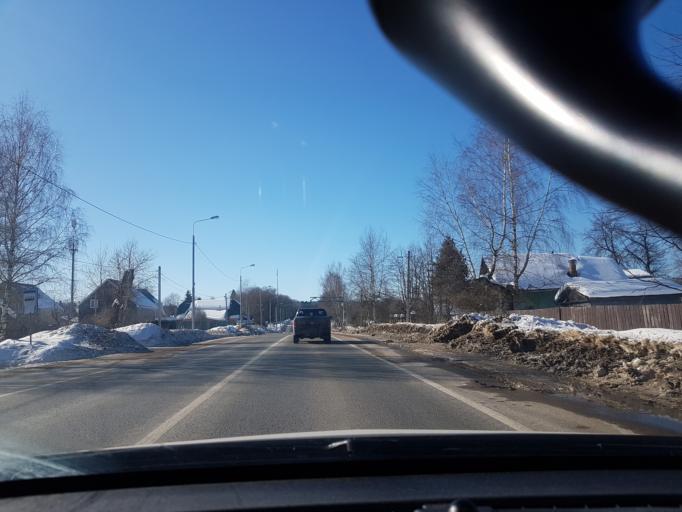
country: RU
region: Moskovskaya
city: Kostrovo
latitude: 55.9170
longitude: 36.6819
